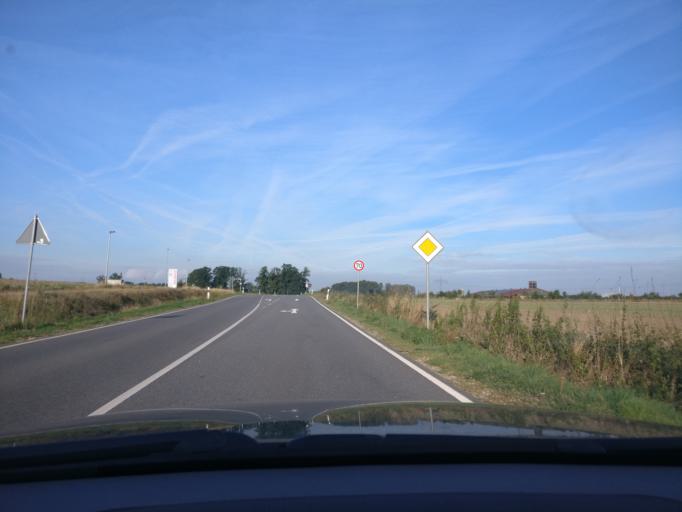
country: DE
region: Lower Saxony
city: Melle
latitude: 52.1996
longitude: 8.3055
